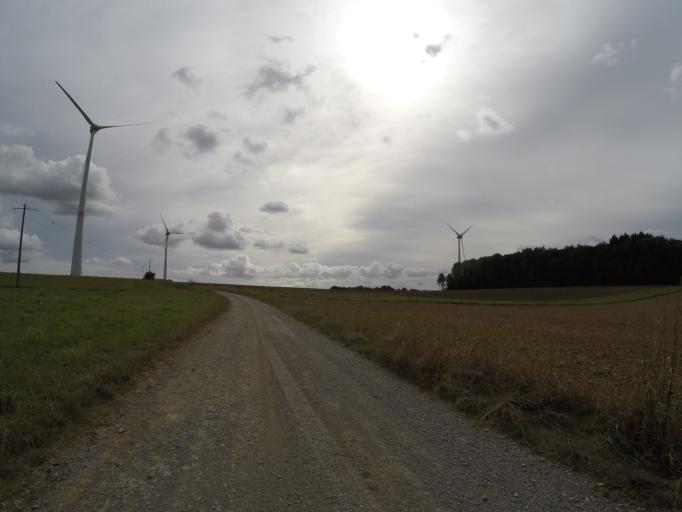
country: BE
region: Wallonia
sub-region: Province de Namur
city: Assesse
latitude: 50.3004
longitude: 4.9816
